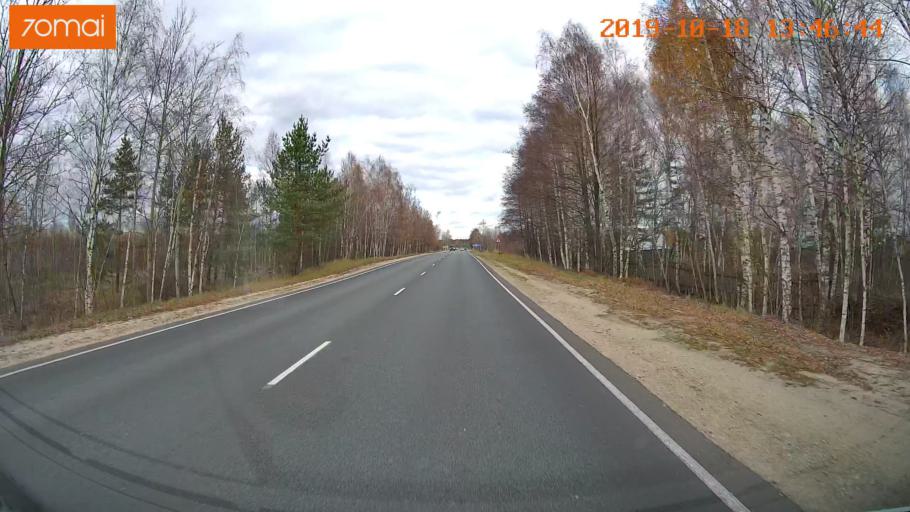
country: RU
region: Rjazan
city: Solotcha
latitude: 54.9650
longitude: 39.9462
